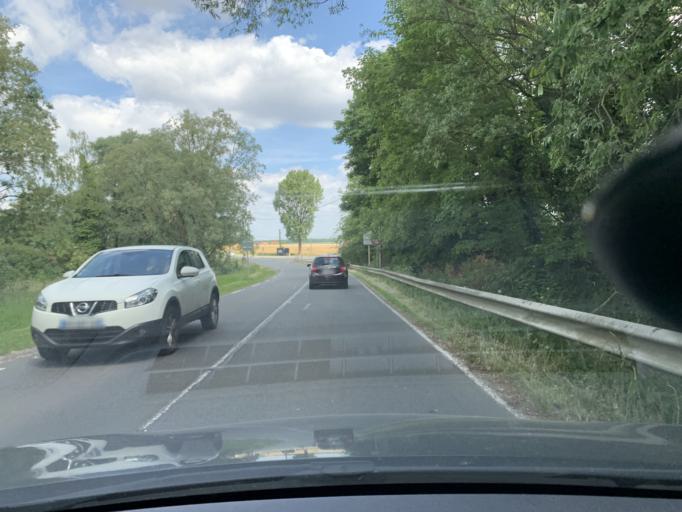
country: FR
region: Nord-Pas-de-Calais
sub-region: Departement du Nord
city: Goeulzin
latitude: 50.3072
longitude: 3.0986
